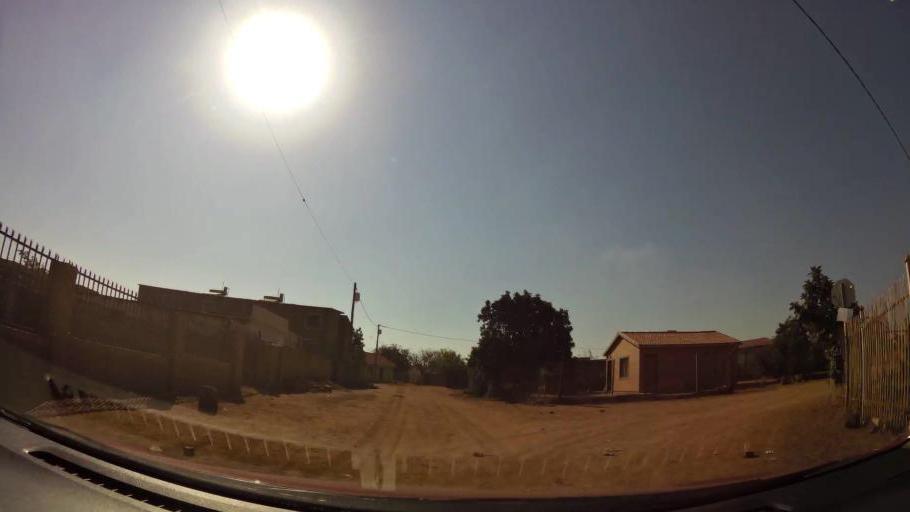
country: ZA
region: Gauteng
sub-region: City of Tshwane Metropolitan Municipality
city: Mabopane
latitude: -25.5500
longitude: 28.0840
